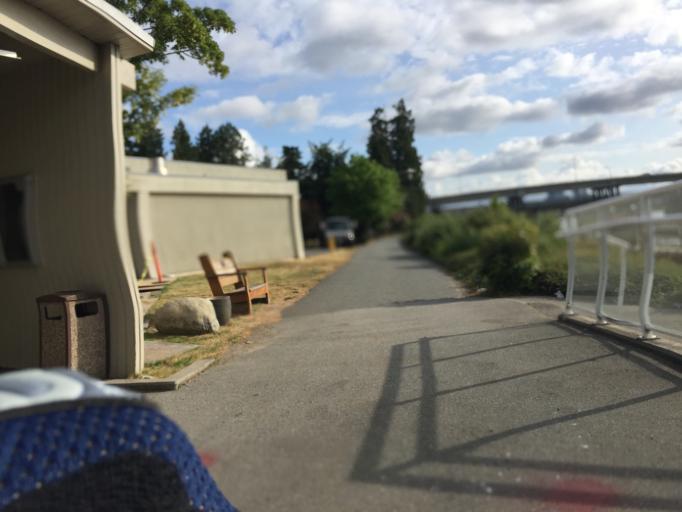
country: CA
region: British Columbia
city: Richmond
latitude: 49.1909
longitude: -123.1397
